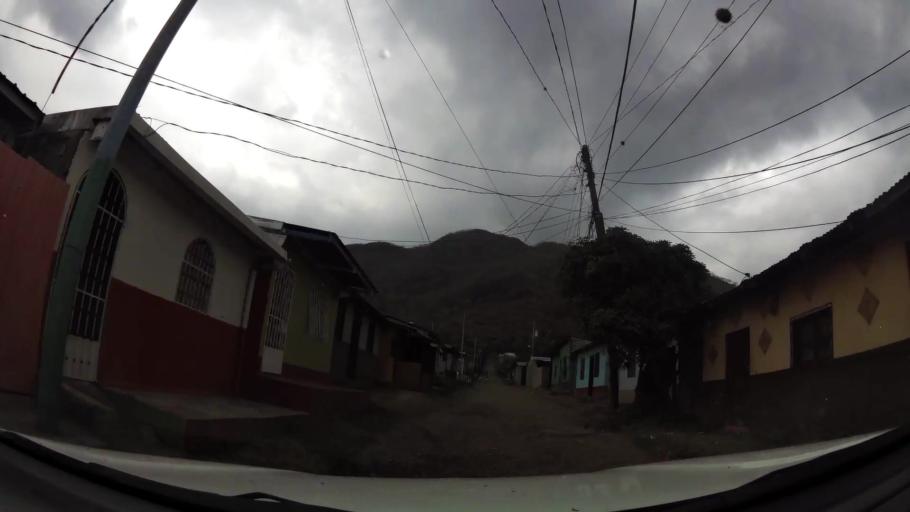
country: NI
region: Jinotega
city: Jinotega
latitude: 13.0979
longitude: -86.0057
